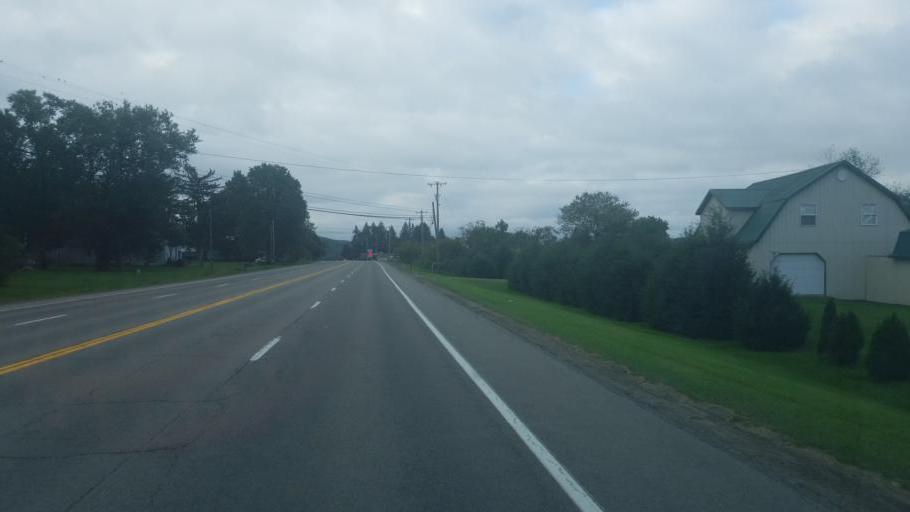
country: US
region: New York
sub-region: Cattaraugus County
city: Weston Mills
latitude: 42.1543
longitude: -78.3976
